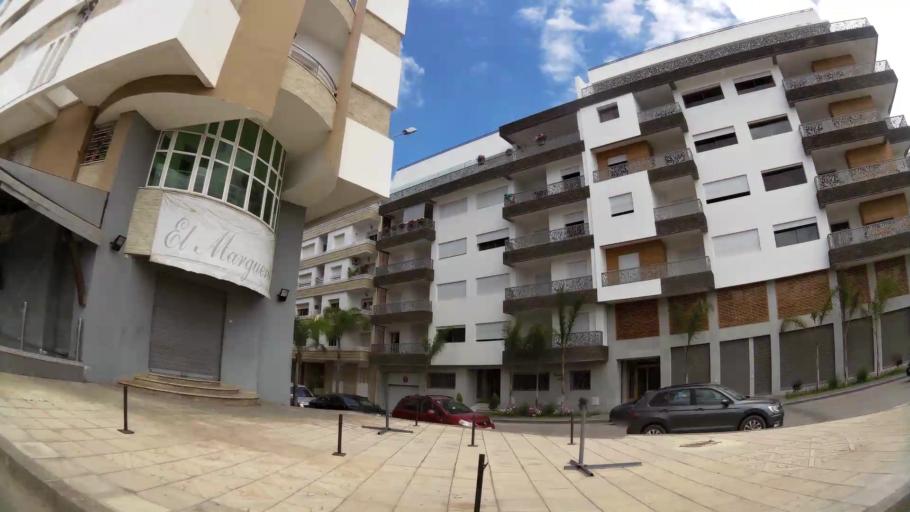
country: MA
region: Gharb-Chrarda-Beni Hssen
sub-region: Kenitra Province
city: Kenitra
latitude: 34.2527
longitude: -6.5915
